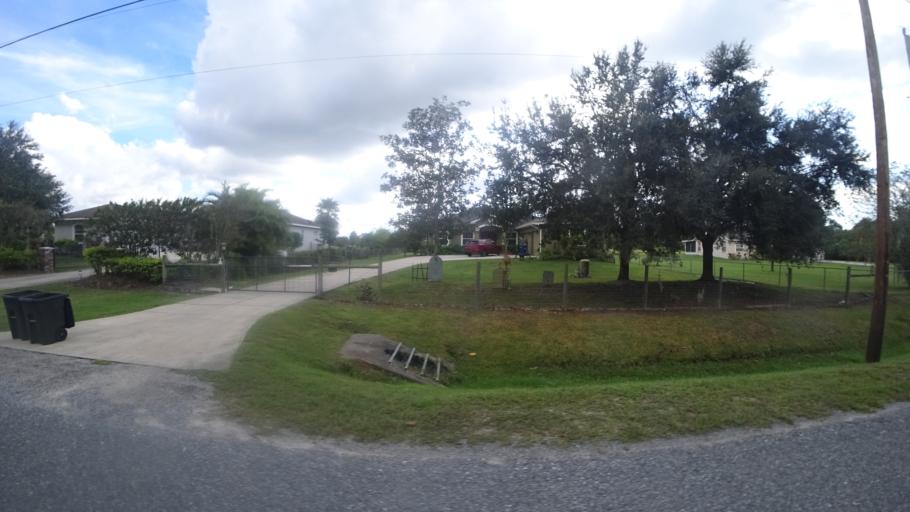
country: US
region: Florida
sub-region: Manatee County
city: Memphis
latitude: 27.6161
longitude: -82.5306
